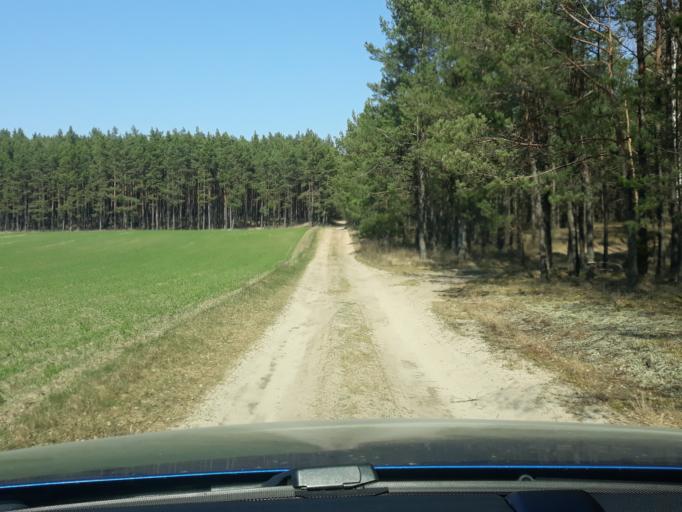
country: PL
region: Pomeranian Voivodeship
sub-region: Powiat bytowski
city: Lipnica
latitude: 53.8529
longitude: 17.4321
